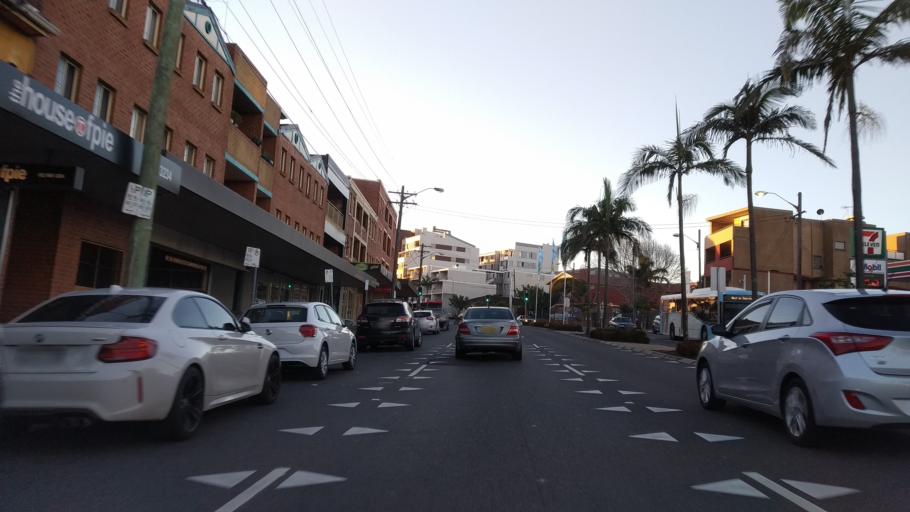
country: AU
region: New South Wales
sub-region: Randwick
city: Maroubra
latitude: -33.9598
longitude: 151.2313
